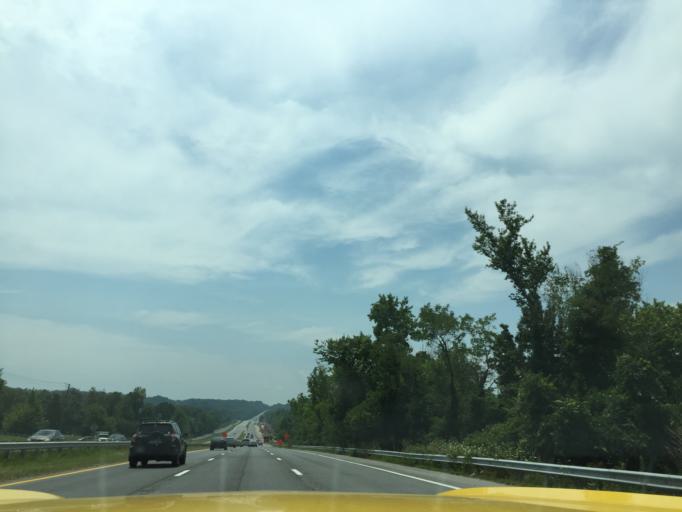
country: US
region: Maryland
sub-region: Prince George's County
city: Friendly
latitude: 38.7412
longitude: -76.9917
